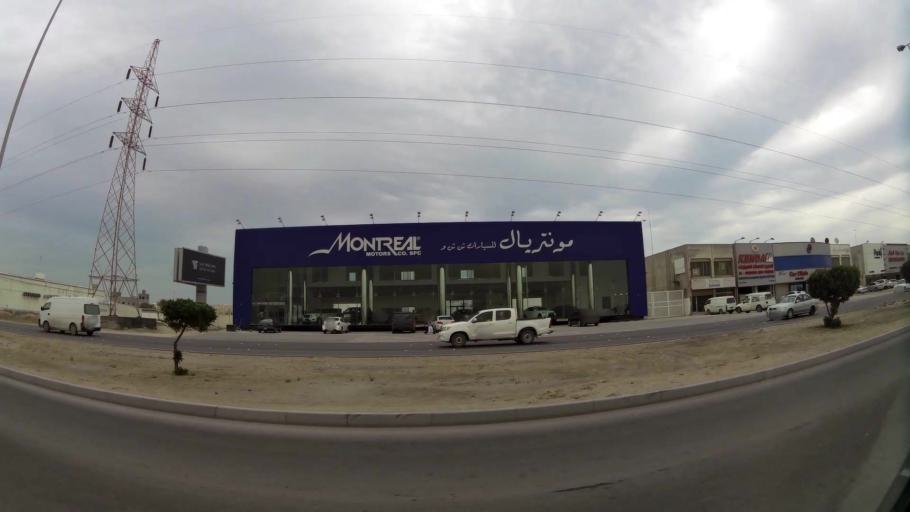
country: BH
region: Northern
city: Sitrah
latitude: 26.1540
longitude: 50.6130
